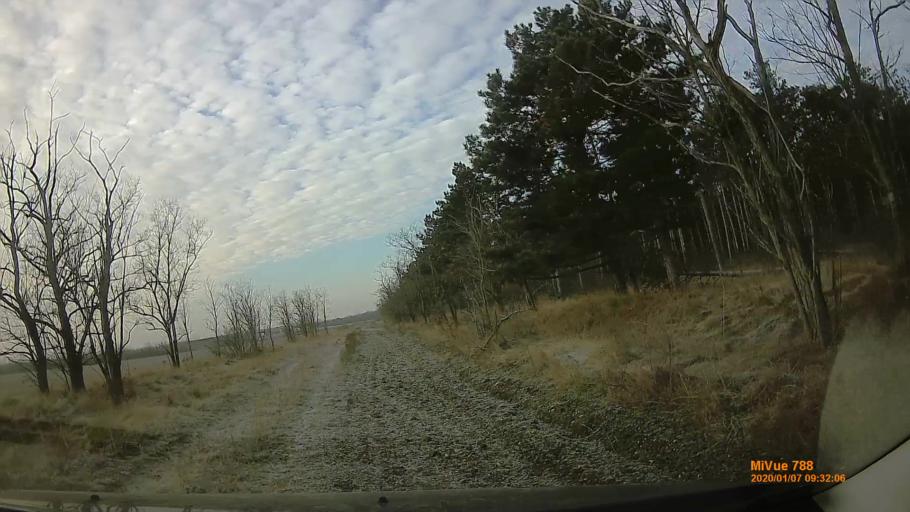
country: HU
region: Gyor-Moson-Sopron
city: Rajka
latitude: 47.9449
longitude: 17.1713
